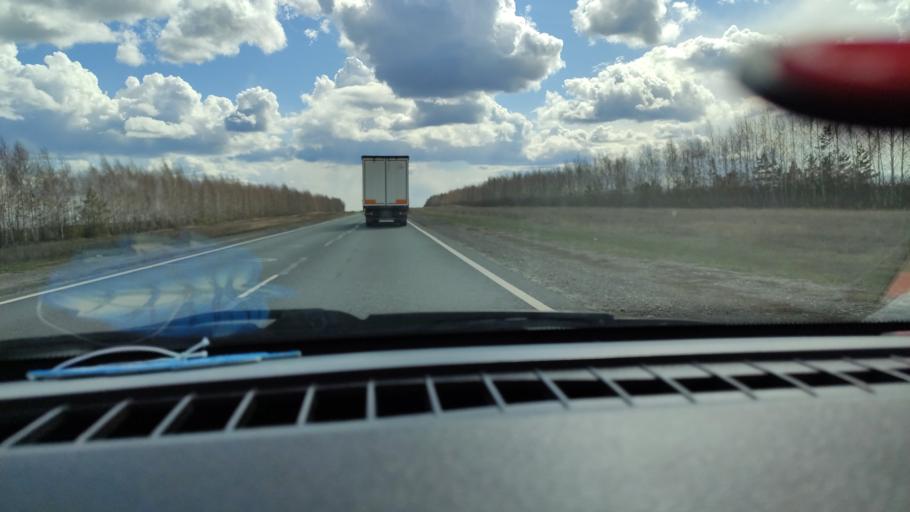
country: RU
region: Saratov
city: Dukhovnitskoye
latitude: 52.8146
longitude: 48.2310
